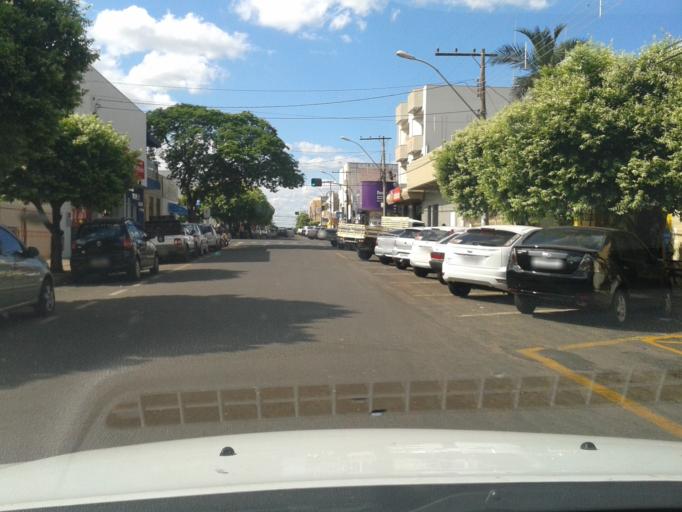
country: BR
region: Minas Gerais
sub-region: Iturama
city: Iturama
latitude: -19.7304
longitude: -50.1980
